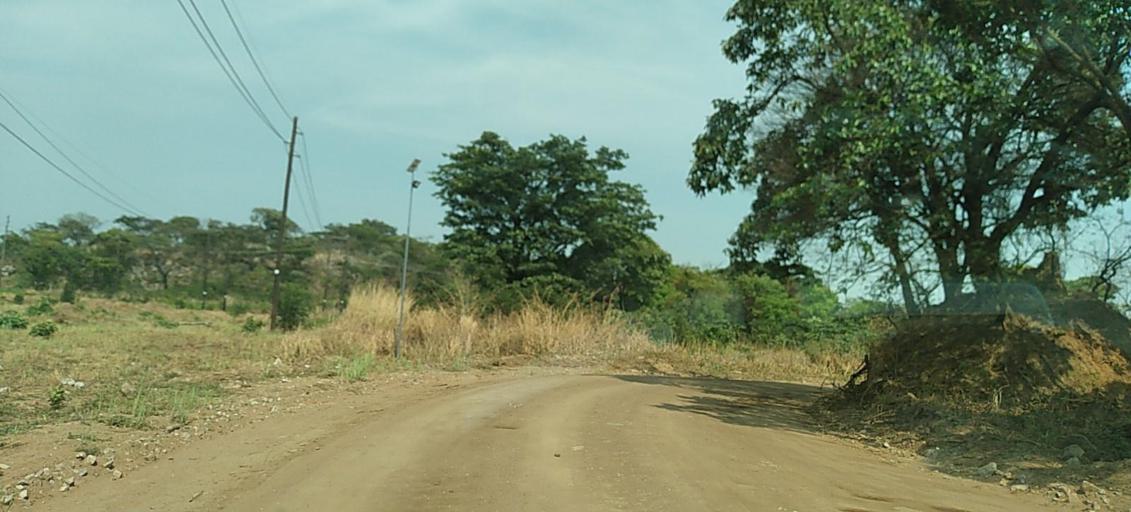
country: ZM
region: Copperbelt
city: Chililabombwe
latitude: -12.2950
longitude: 27.7699
